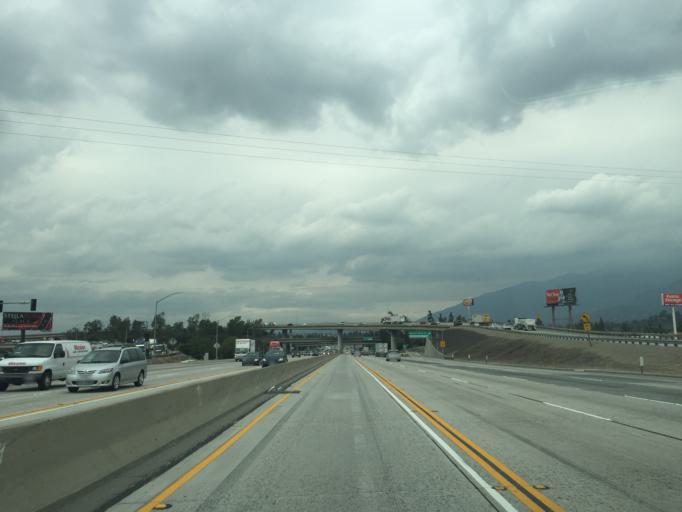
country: US
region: California
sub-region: Los Angeles County
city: Bradbury
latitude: 34.1332
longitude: -117.9530
